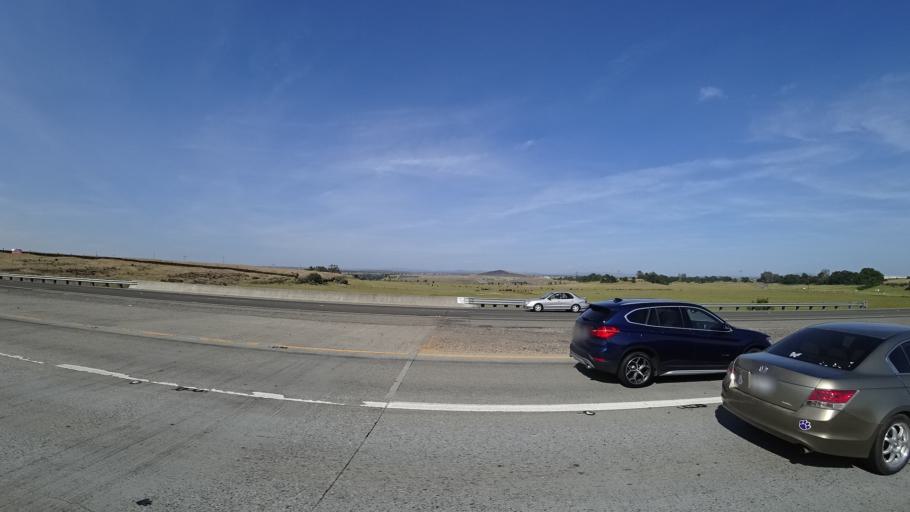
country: US
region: California
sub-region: Butte County
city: Durham
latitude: 39.6667
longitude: -121.7453
